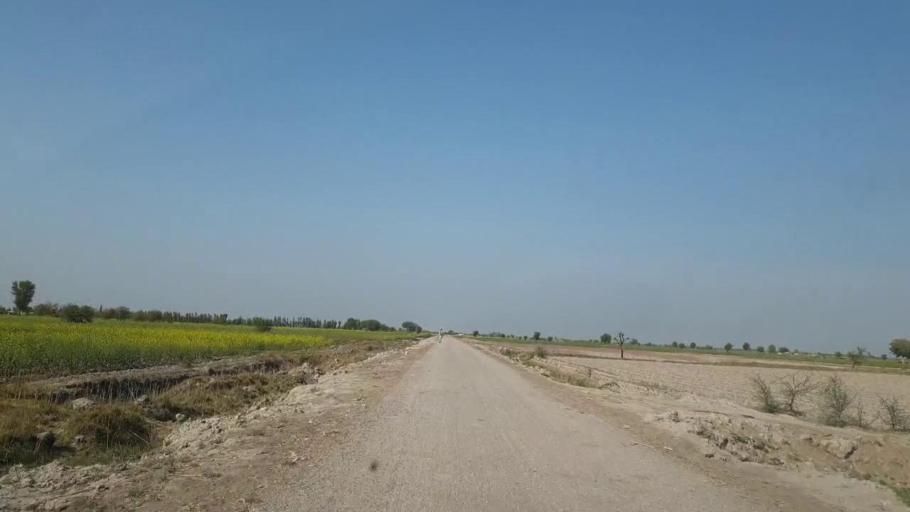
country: PK
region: Sindh
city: Mirpur Khas
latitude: 25.7277
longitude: 69.1614
